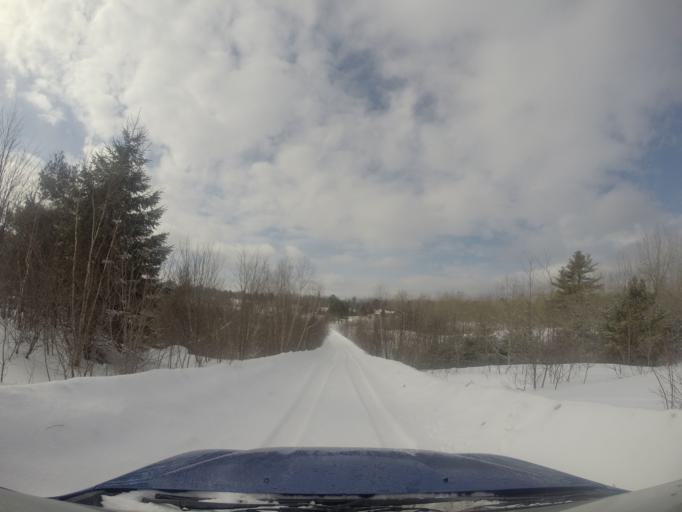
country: CA
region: Ontario
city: Greater Sudbury
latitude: 46.1045
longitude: -80.6790
